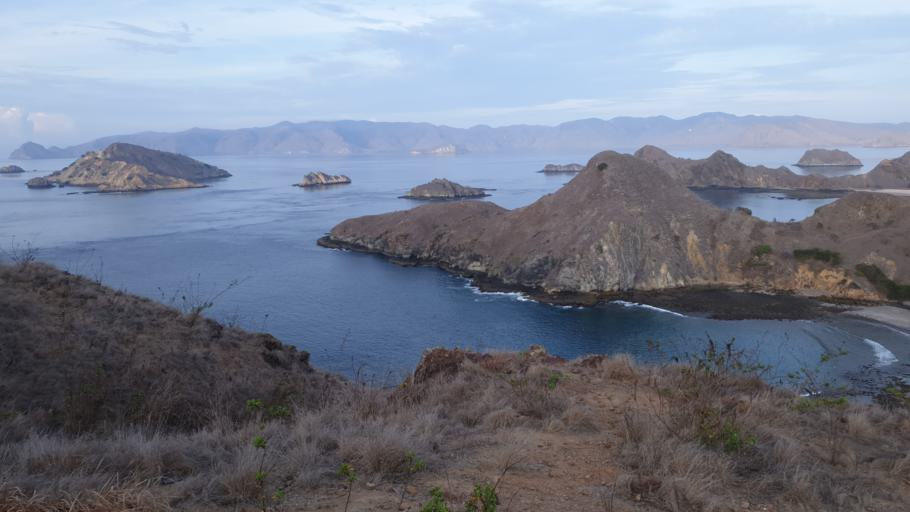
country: ID
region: East Nusa Tenggara
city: Komodo
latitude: -8.6797
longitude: 119.5565
